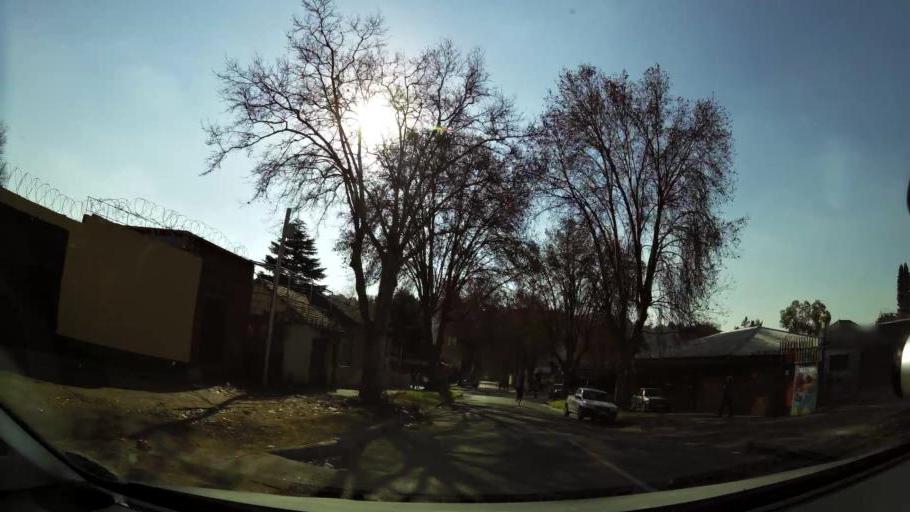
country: ZA
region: Gauteng
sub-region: City of Johannesburg Metropolitan Municipality
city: Johannesburg
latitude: -26.1932
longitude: 28.0791
